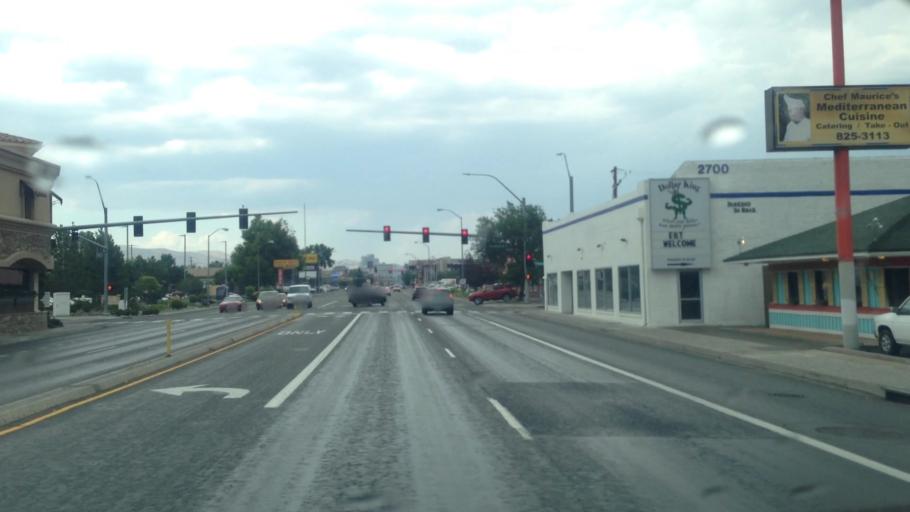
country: US
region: Nevada
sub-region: Washoe County
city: Reno
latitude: 39.4982
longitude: -119.7995
